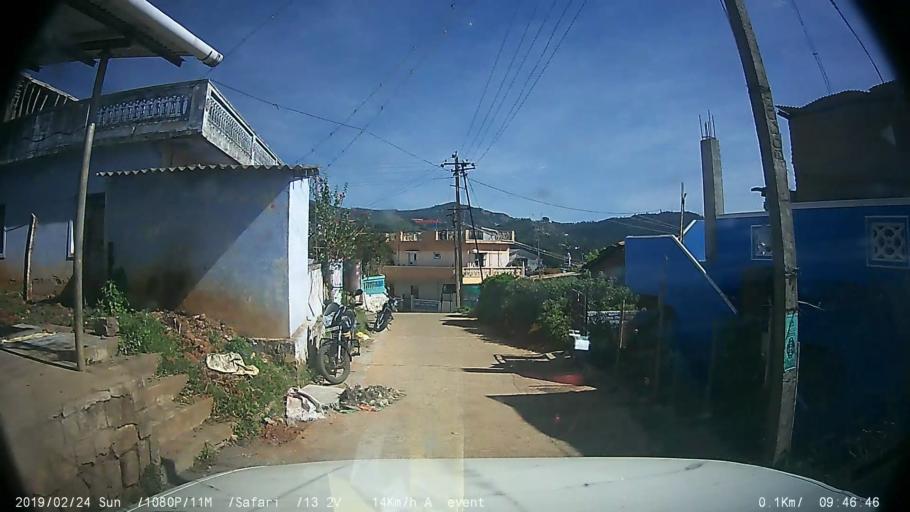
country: IN
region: Tamil Nadu
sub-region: Nilgiri
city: Wellington
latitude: 11.3467
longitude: 76.7796
